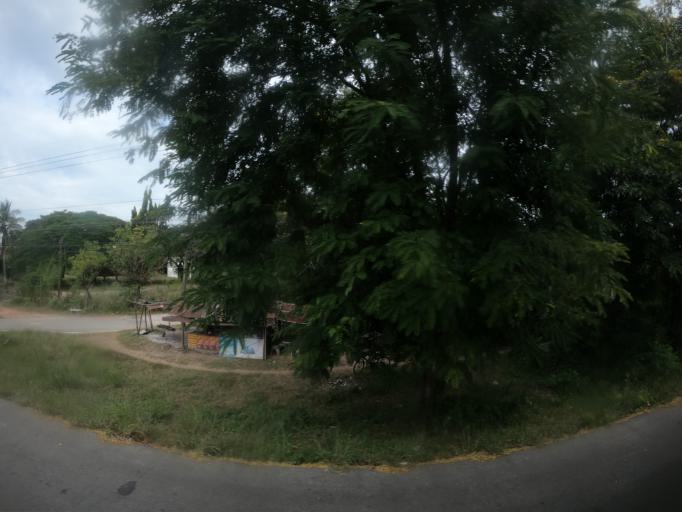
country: TH
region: Maha Sarakham
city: Maha Sarakham
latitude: 16.1478
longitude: 103.4033
